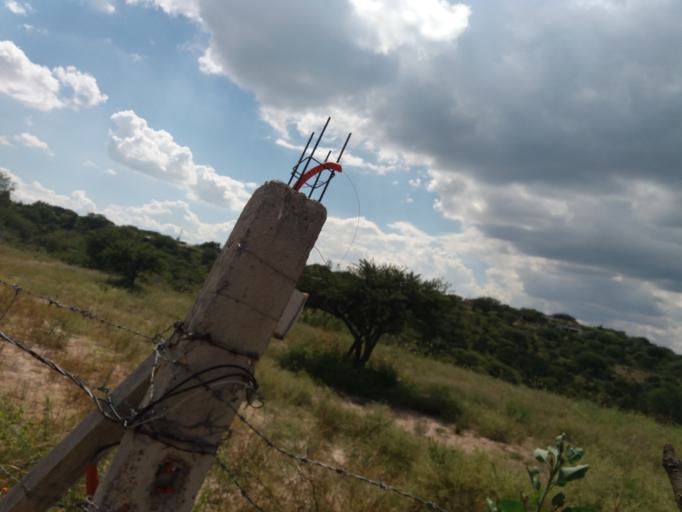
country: MX
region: Aguascalientes
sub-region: Aguascalientes
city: San Sebastian [Fraccionamiento]
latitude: 21.8006
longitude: -102.2426
